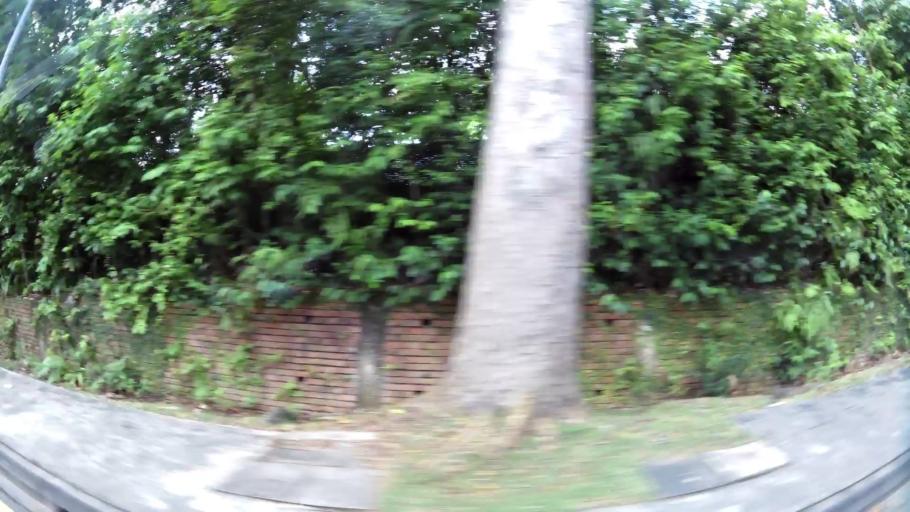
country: SG
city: Singapore
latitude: 1.3353
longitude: 103.7984
